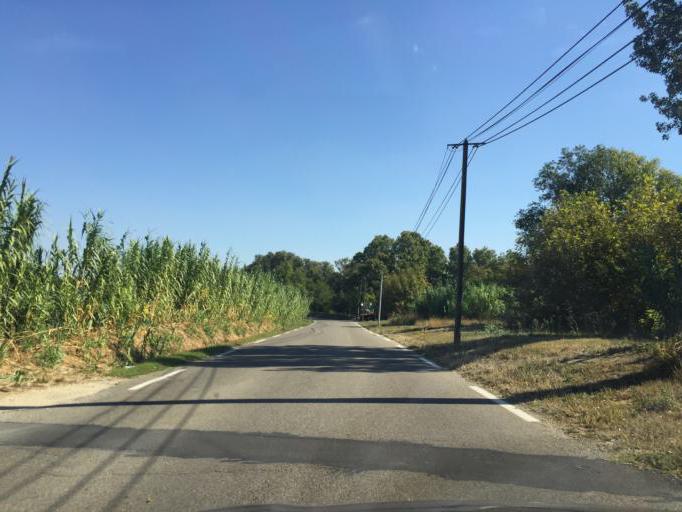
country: FR
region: Provence-Alpes-Cote d'Azur
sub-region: Departement du Vaucluse
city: Monteux
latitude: 44.0397
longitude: 4.9793
